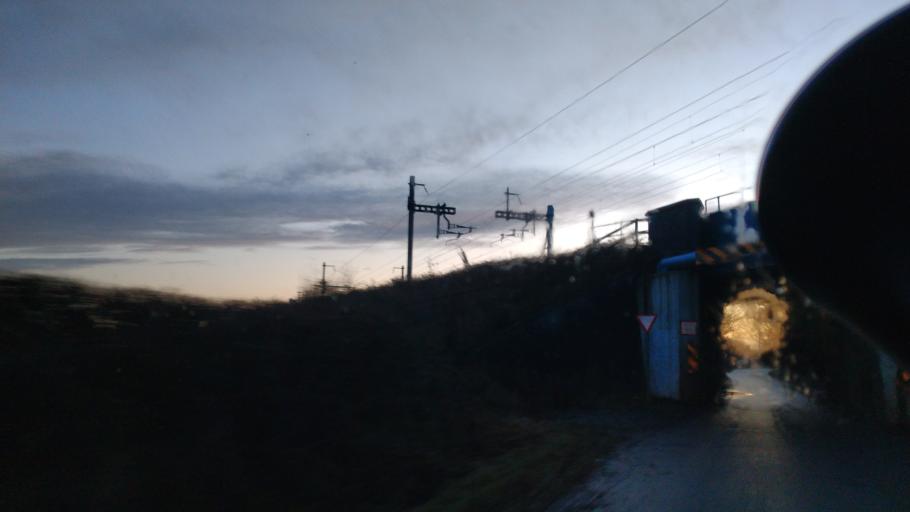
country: GB
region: England
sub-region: Borough of Swindon
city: Wanborough
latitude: 51.5835
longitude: -1.7088
